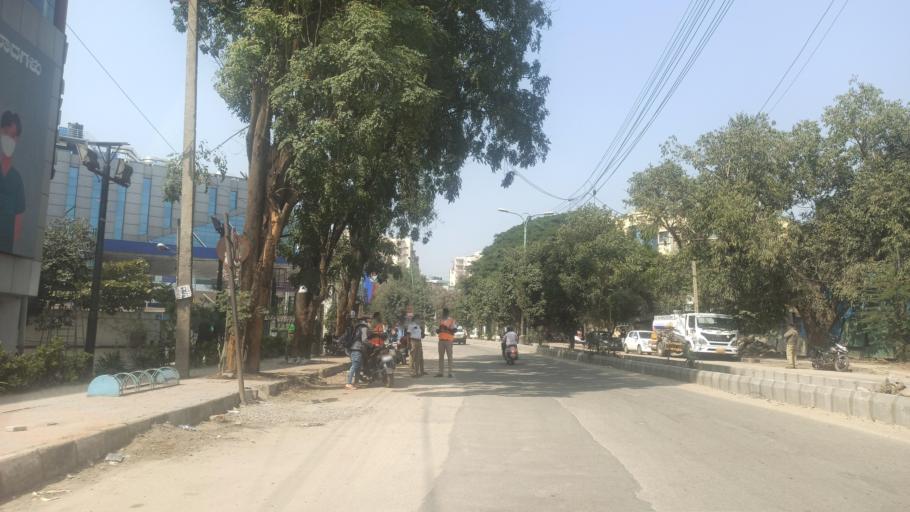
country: IN
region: Karnataka
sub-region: Bangalore Urban
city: Bangalore
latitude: 12.9663
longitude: 77.7181
